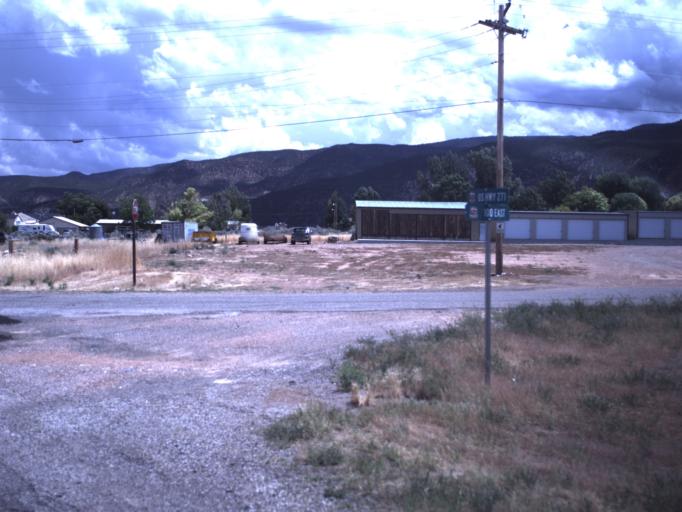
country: US
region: Utah
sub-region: Iron County
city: Parowan
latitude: 37.8520
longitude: -112.8259
